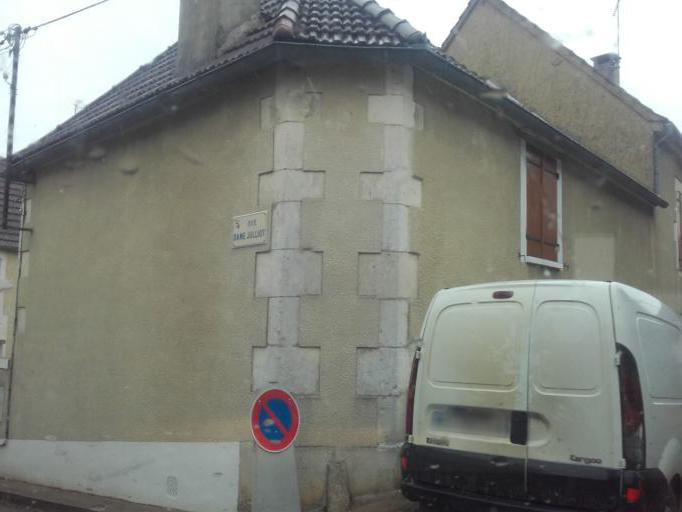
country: FR
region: Bourgogne
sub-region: Departement de l'Yonne
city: Chablis
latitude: 47.7745
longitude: 3.7547
